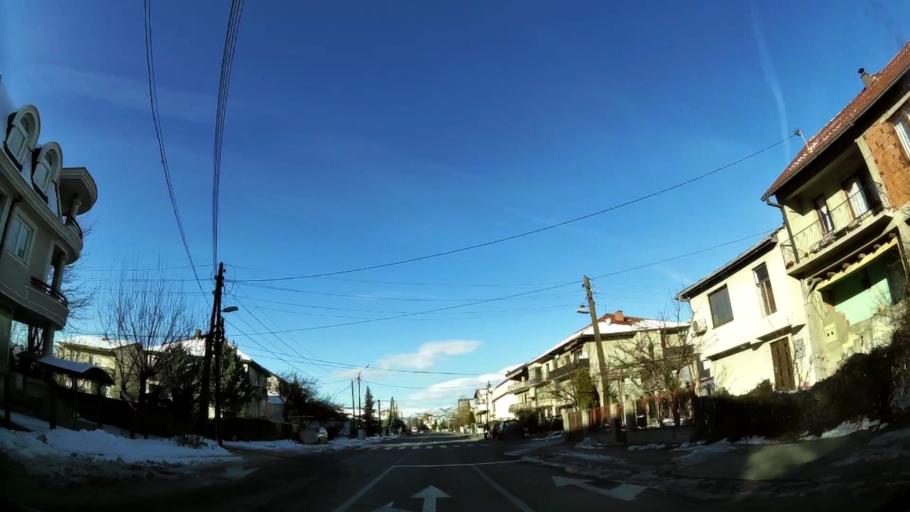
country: MK
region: Saraj
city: Saraj
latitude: 42.0089
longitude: 21.3562
